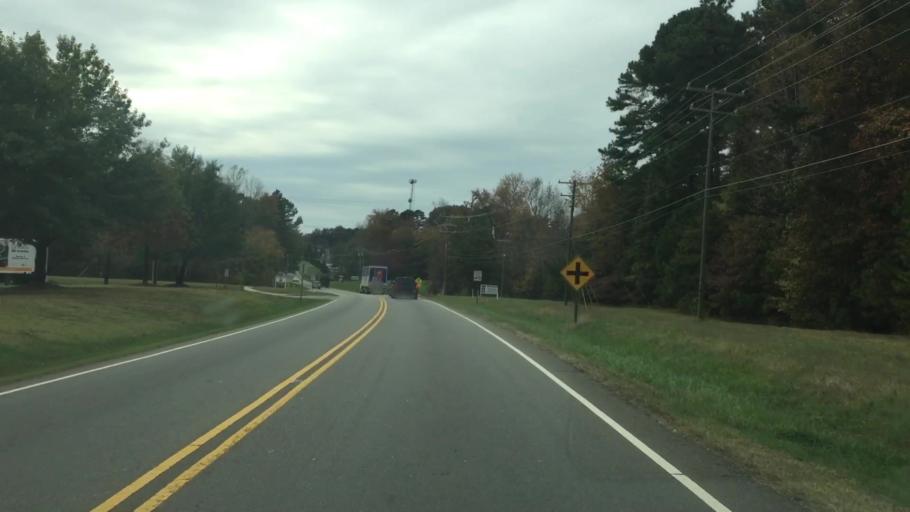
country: US
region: North Carolina
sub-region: Iredell County
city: Mooresville
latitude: 35.6084
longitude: -80.7988
